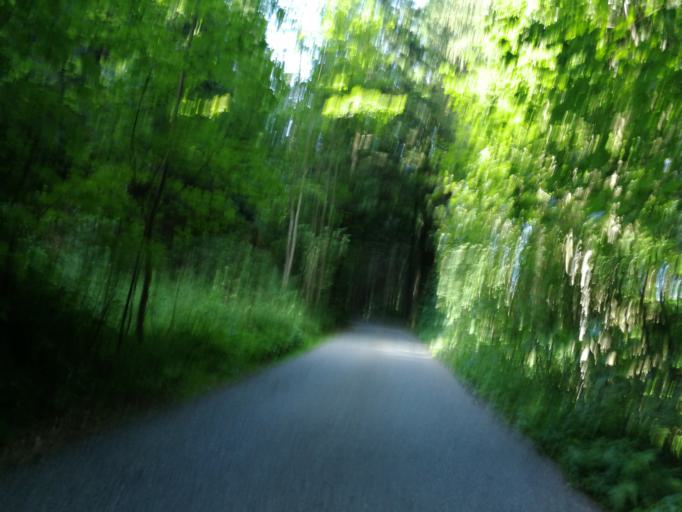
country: CH
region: Saint Gallen
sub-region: Wahlkreis See-Gaster
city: Gommiswald
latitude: 47.2534
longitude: 9.0410
